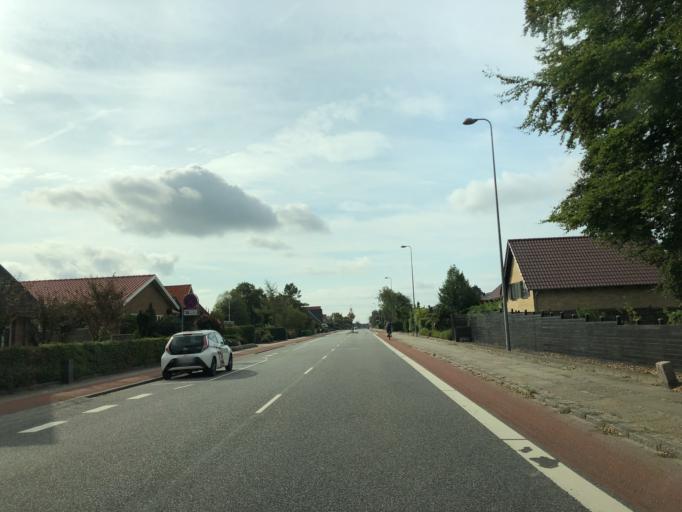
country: DK
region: Central Jutland
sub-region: Ringkobing-Skjern Kommune
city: Skjern
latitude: 55.9387
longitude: 8.5029
